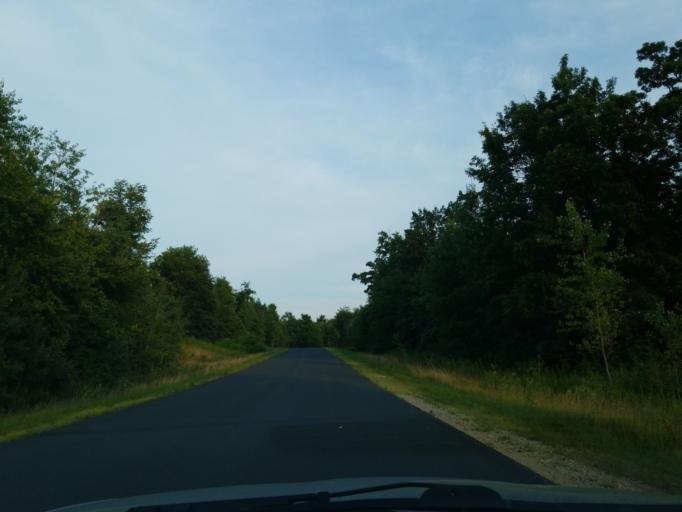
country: US
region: Minnesota
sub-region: Washington County
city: Stillwater
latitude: 45.0682
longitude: -92.7751
